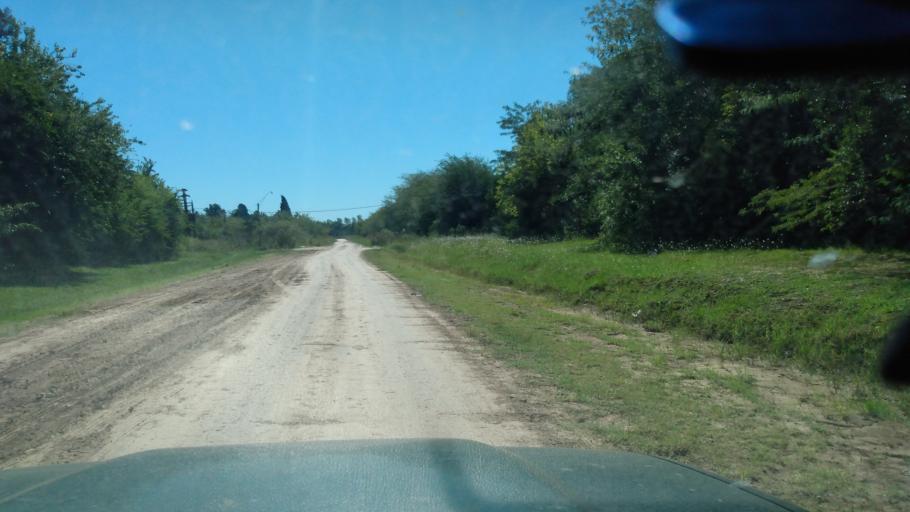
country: AR
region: Buenos Aires
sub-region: Partido de Lujan
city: Lujan
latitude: -34.5530
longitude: -59.1448
